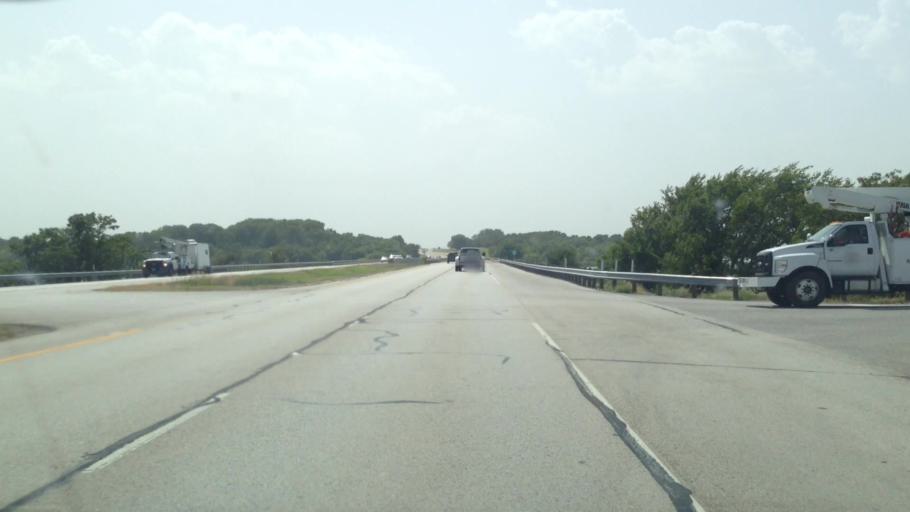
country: US
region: Texas
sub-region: Collin County
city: Princeton
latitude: 33.1630
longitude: -96.4317
